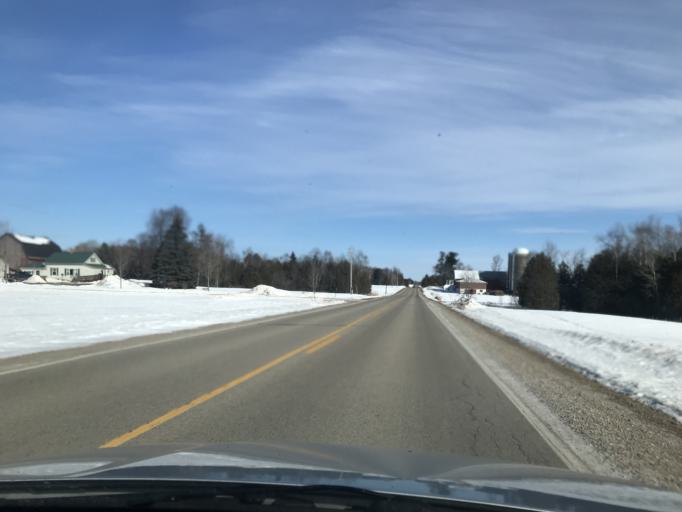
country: US
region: Wisconsin
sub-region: Oconto County
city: Oconto Falls
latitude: 44.9118
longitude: -88.1551
